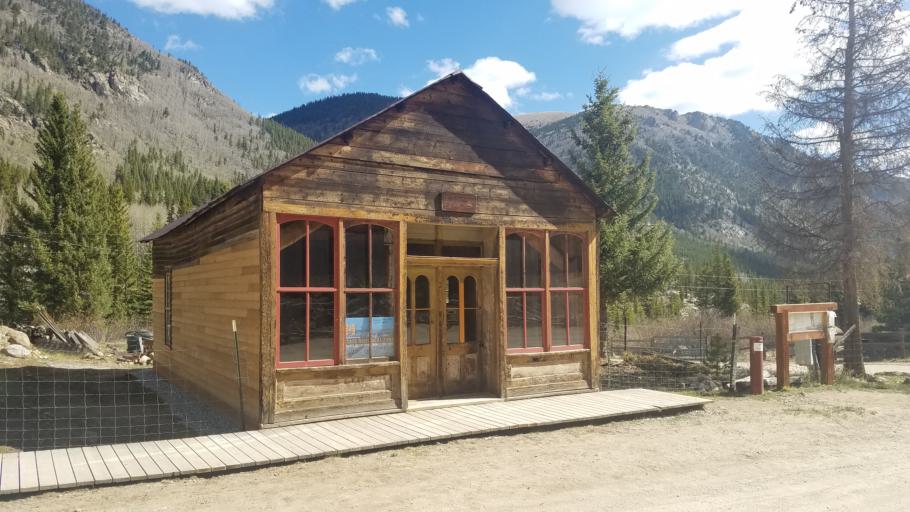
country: US
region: Colorado
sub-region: Chaffee County
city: Buena Vista
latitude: 38.7034
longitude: -106.3465
